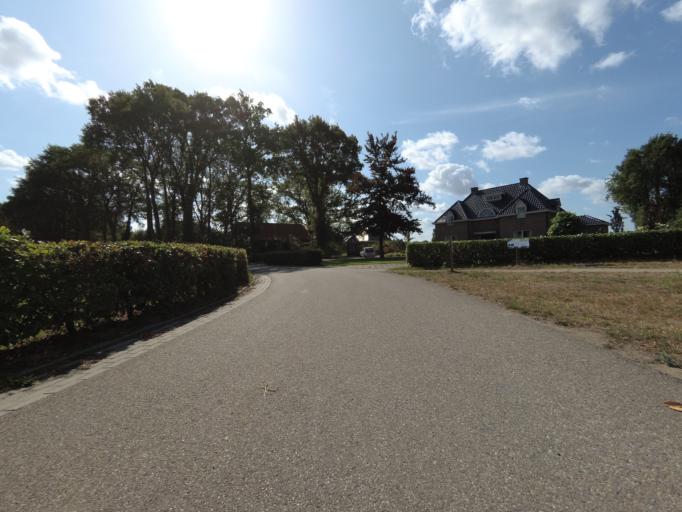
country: NL
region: Overijssel
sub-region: Gemeente Haaksbergen
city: Haaksbergen
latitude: 52.1523
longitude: 6.7616
